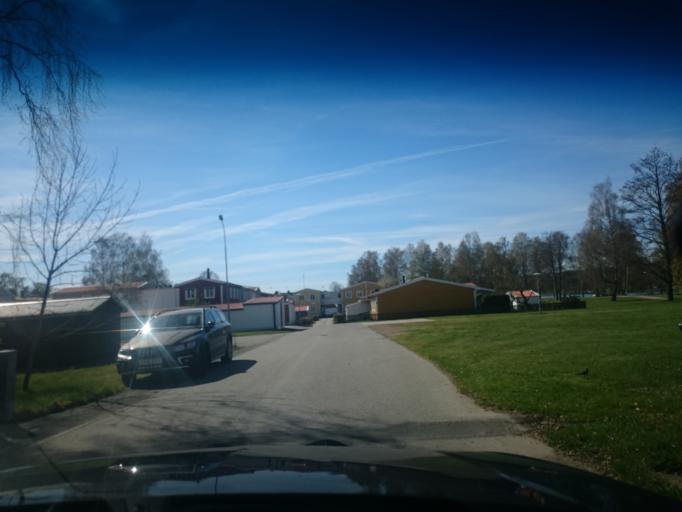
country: SE
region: Kalmar
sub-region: Hultsfreds Kommun
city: Virserum
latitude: 57.3172
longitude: 15.5828
